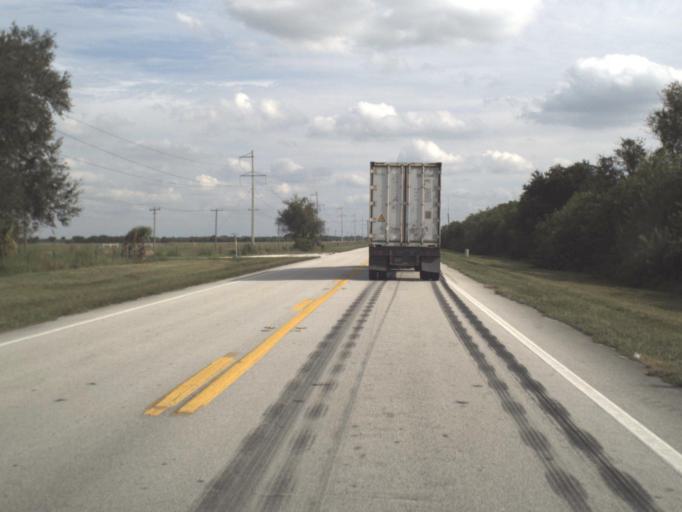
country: US
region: Florida
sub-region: Okeechobee County
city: Taylor Creek
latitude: 27.1963
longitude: -80.7337
